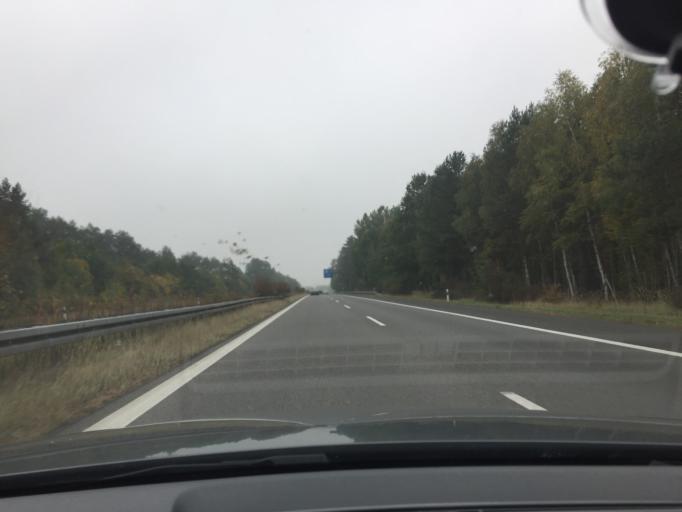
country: DE
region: Brandenburg
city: Calau
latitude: 51.7982
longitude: 13.8832
